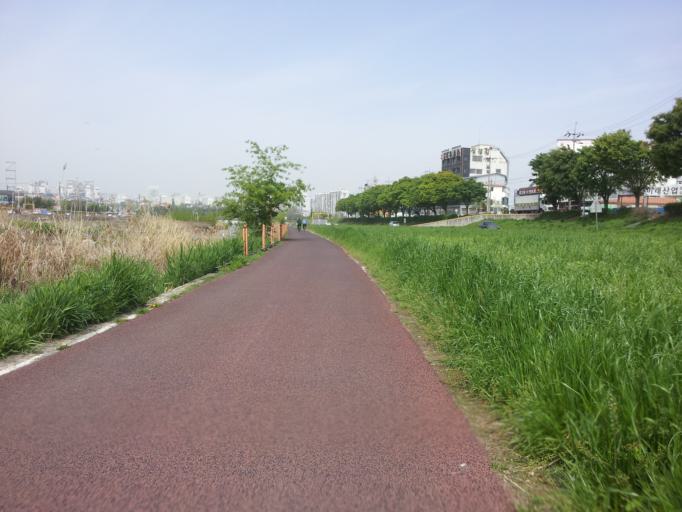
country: KR
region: Daejeon
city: Daejeon
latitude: 36.3486
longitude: 127.4096
